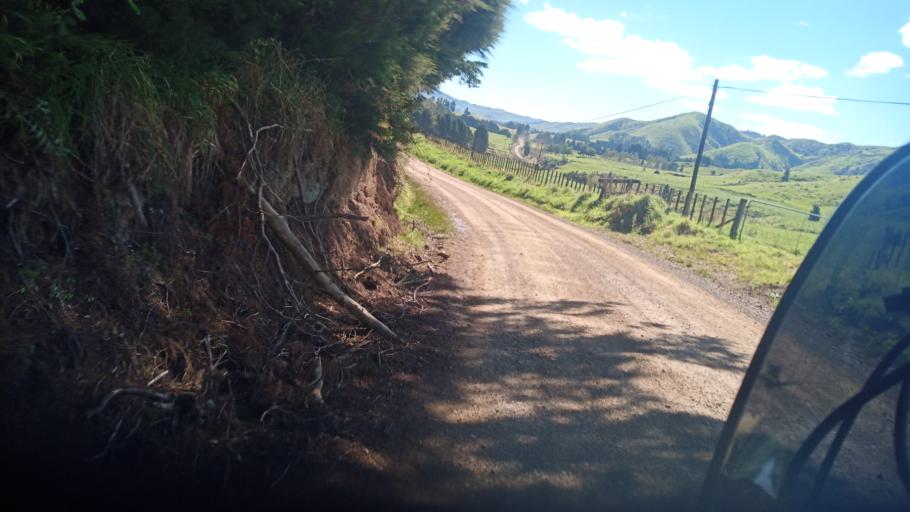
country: NZ
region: Bay of Plenty
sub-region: Opotiki District
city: Opotiki
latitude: -38.3283
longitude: 177.5735
